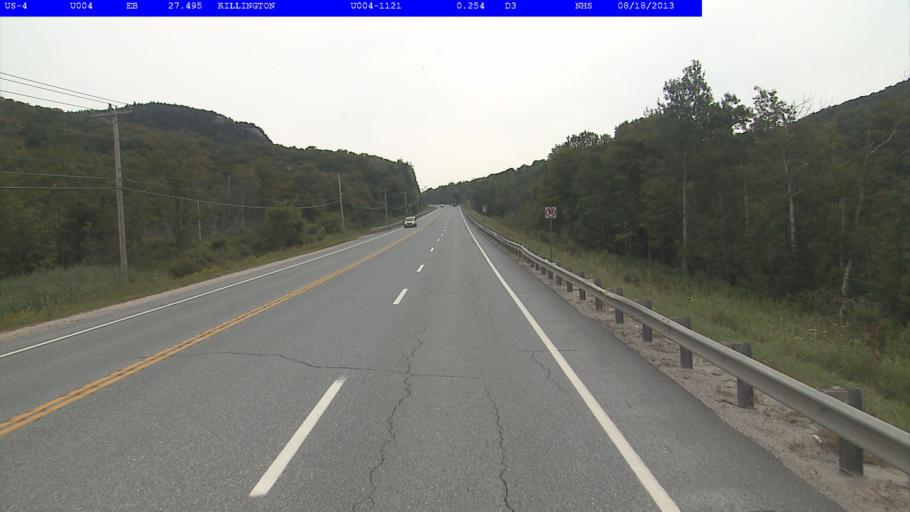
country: US
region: Vermont
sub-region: Rutland County
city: Rutland
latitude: 43.6643
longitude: -72.8415
